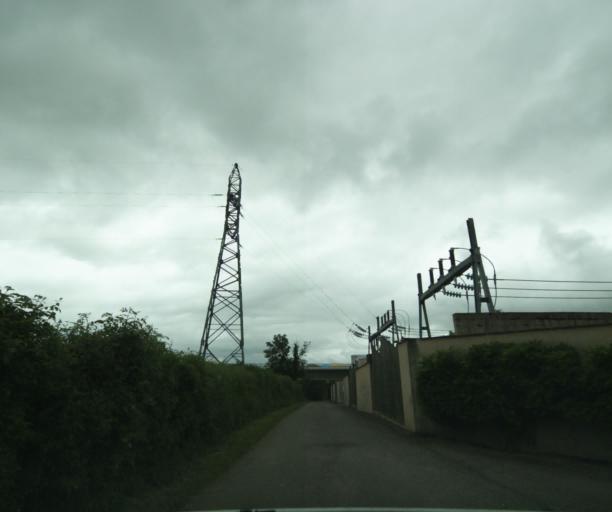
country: FR
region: Bourgogne
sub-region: Departement de Saone-et-Loire
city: Charolles
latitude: 46.4447
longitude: 4.2727
